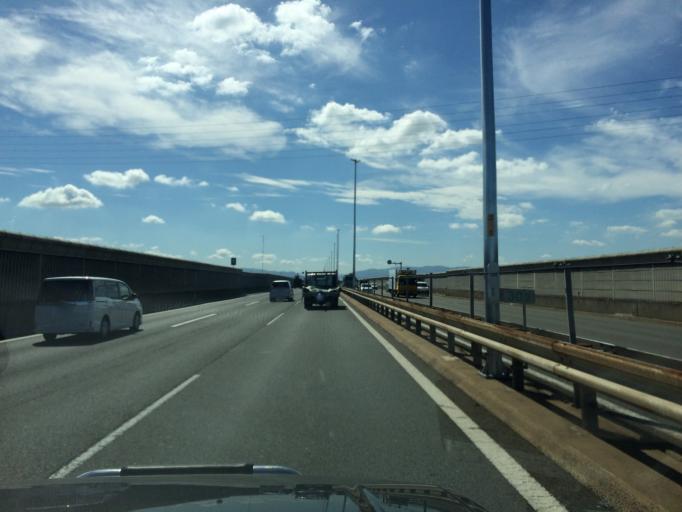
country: JP
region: Osaka
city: Matsubara
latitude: 34.5704
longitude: 135.5639
